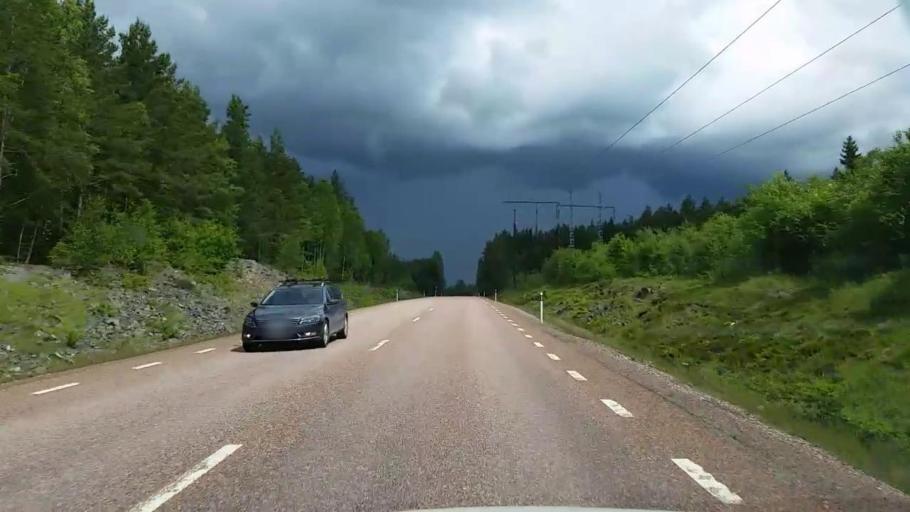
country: SE
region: Gaevleborg
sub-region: Hofors Kommun
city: Hofors
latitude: 60.5439
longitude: 16.4676
